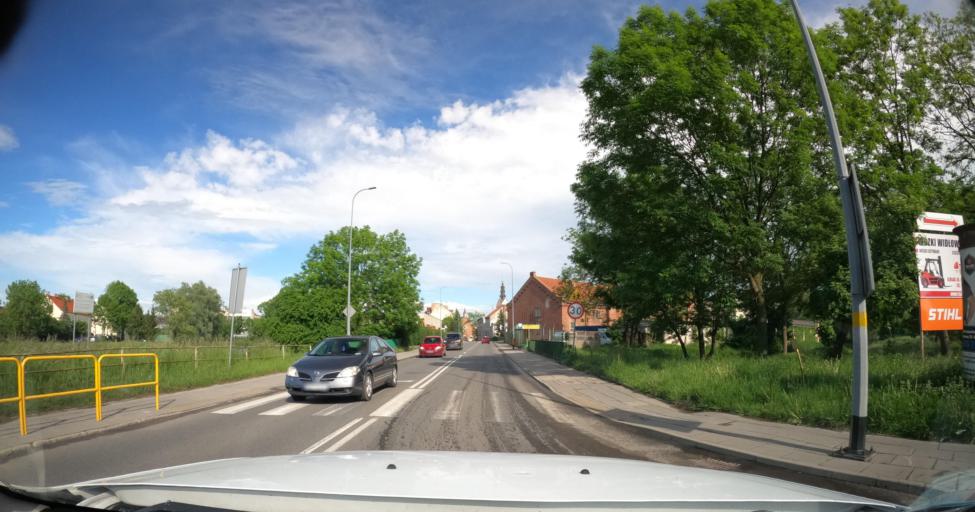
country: PL
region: Warmian-Masurian Voivodeship
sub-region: Powiat elblaski
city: Elblag
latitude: 54.1602
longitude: 19.3863
